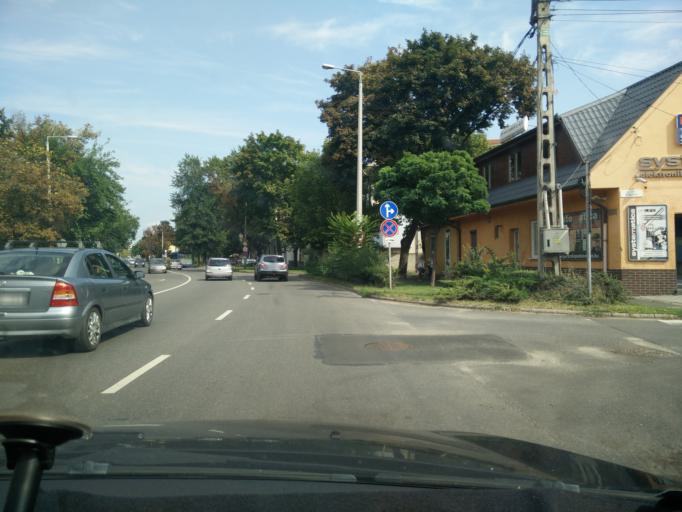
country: HU
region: Hajdu-Bihar
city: Debrecen
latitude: 47.5339
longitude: 21.6139
